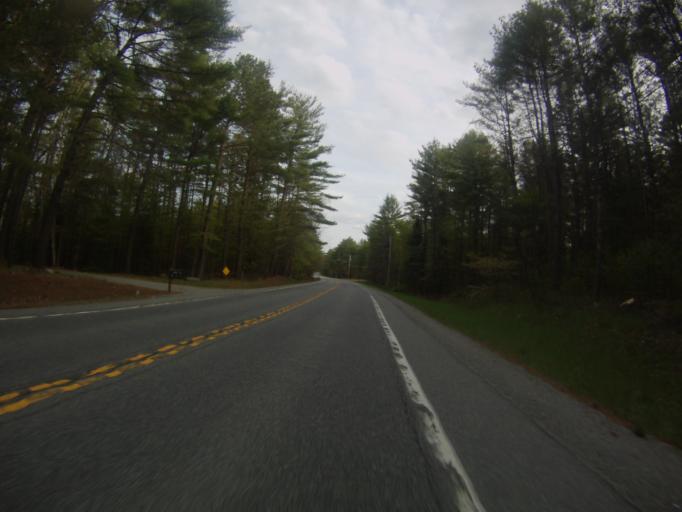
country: US
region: New York
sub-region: Warren County
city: Warrensburg
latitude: 43.6461
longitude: -73.9497
